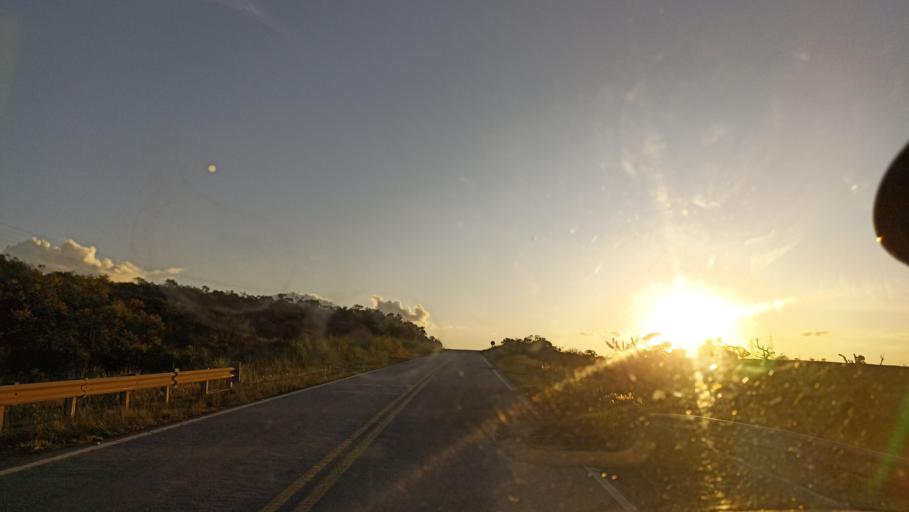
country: BR
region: Minas Gerais
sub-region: Sao Joao Del Rei
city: Sao Joao del Rei
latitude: -21.2245
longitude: -44.3625
